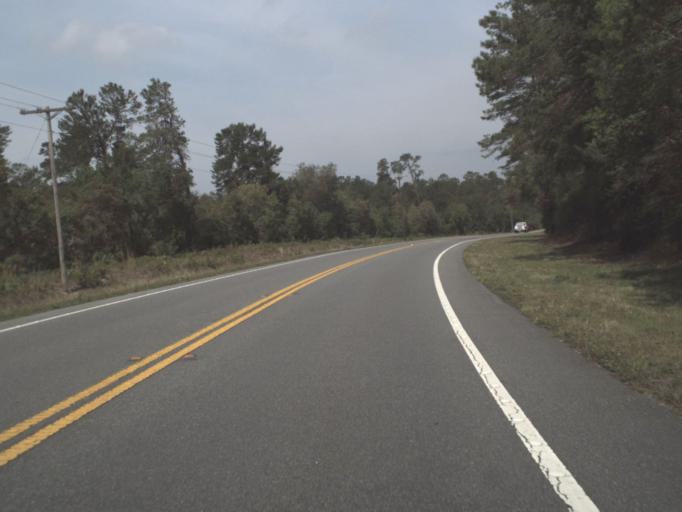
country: US
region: Florida
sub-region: Lake County
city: Astor
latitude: 29.1593
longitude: -81.5996
